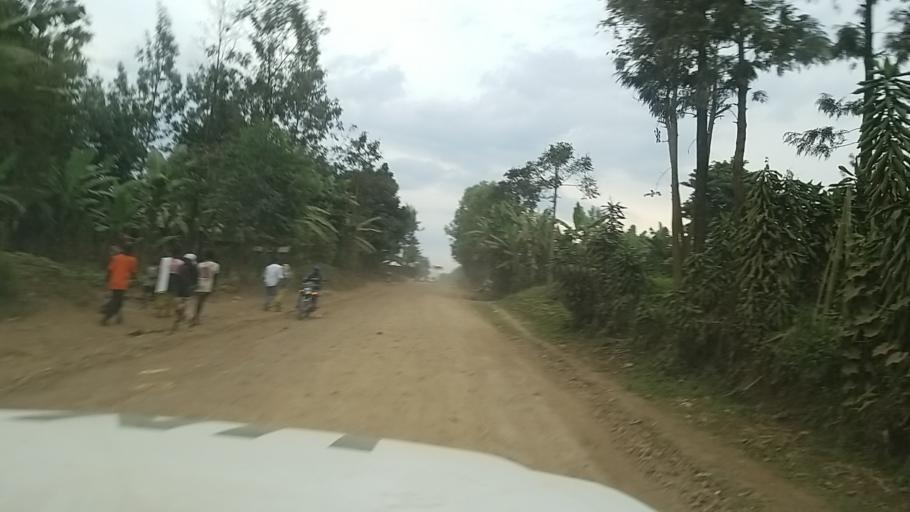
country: CD
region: South Kivu
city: Bukavu
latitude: -2.2733
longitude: 28.8175
